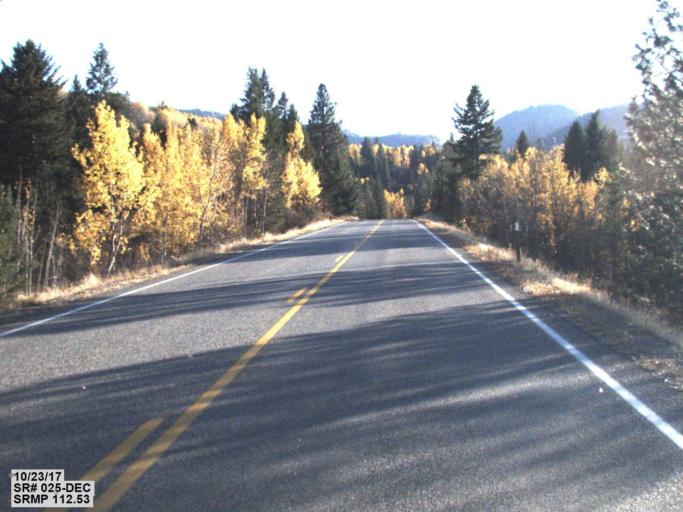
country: CA
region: British Columbia
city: Rossland
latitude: 48.9052
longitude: -117.7932
